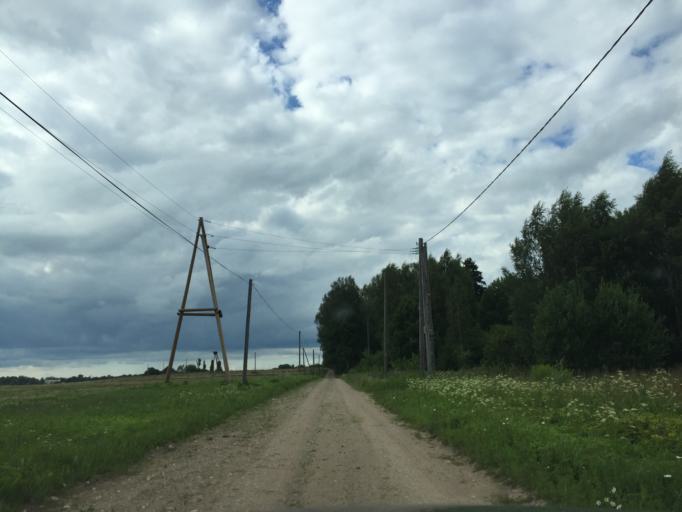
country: LV
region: Malpils
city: Malpils
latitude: 56.9942
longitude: 24.9678
